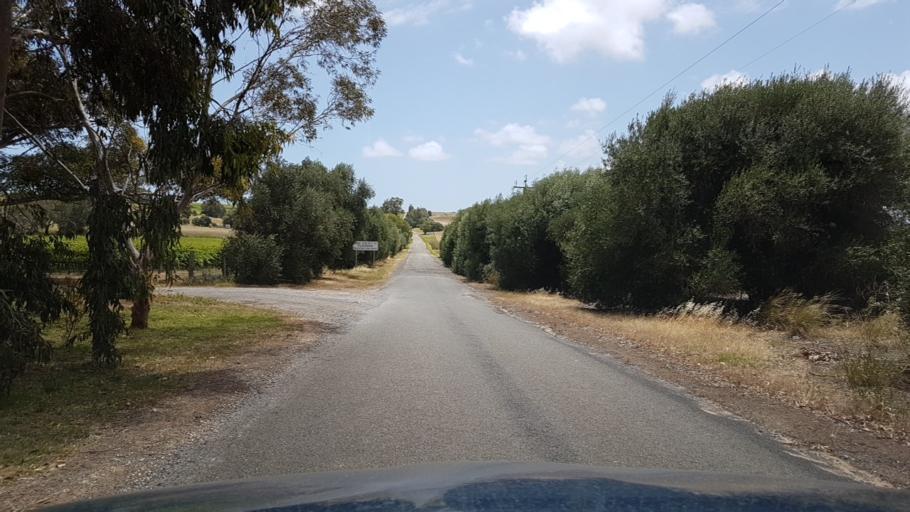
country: AU
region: South Australia
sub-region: Onkaparinga
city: McLaren Vale
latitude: -35.2453
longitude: 138.5329
